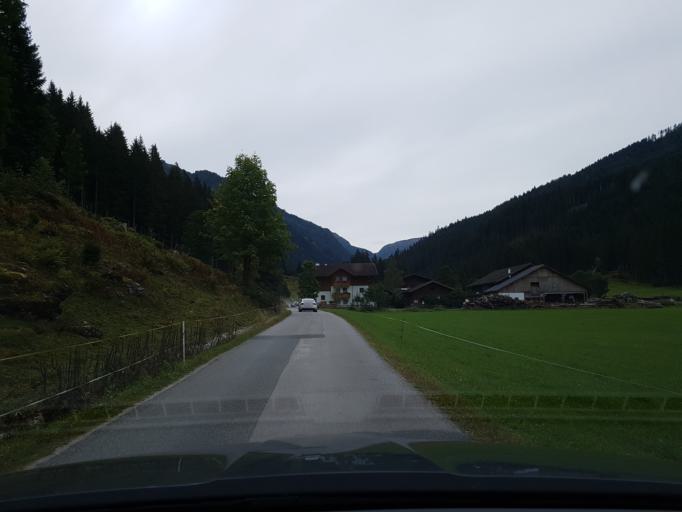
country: AT
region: Salzburg
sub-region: Politischer Bezirk Sankt Johann im Pongau
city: Forstau
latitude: 47.3533
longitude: 13.5717
